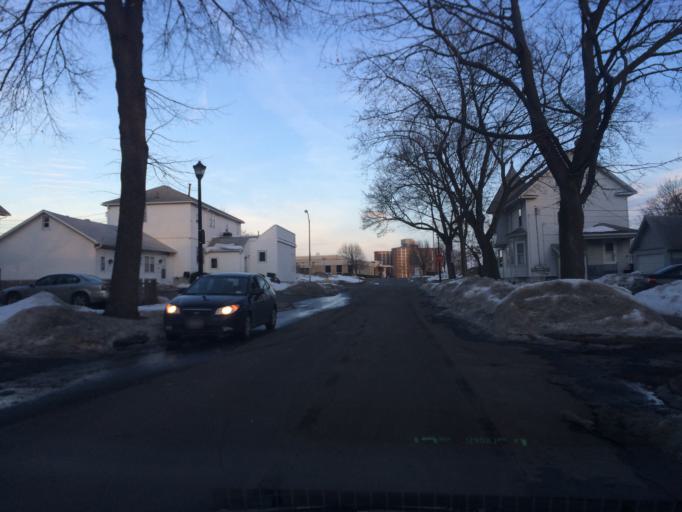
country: US
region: New York
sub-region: Monroe County
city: Rochester
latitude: 43.1260
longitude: -77.6147
